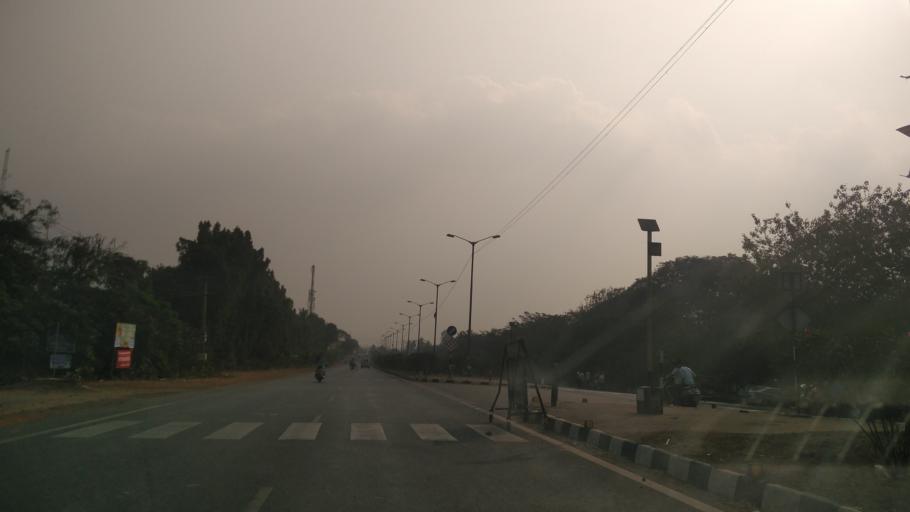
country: IN
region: Andhra Pradesh
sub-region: East Godavari
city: Rajahmundry
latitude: 16.9614
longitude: 81.7948
